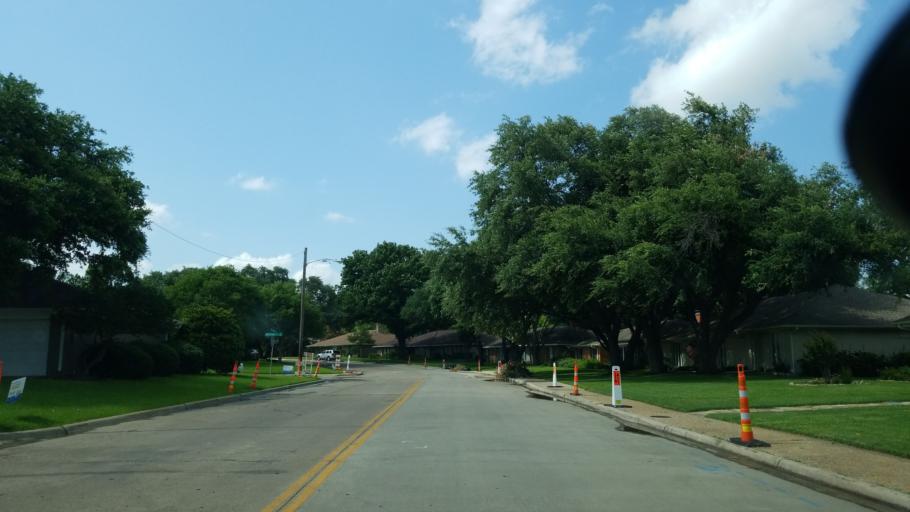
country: US
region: Texas
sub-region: Dallas County
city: Farmers Branch
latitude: 32.8816
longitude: -96.8619
